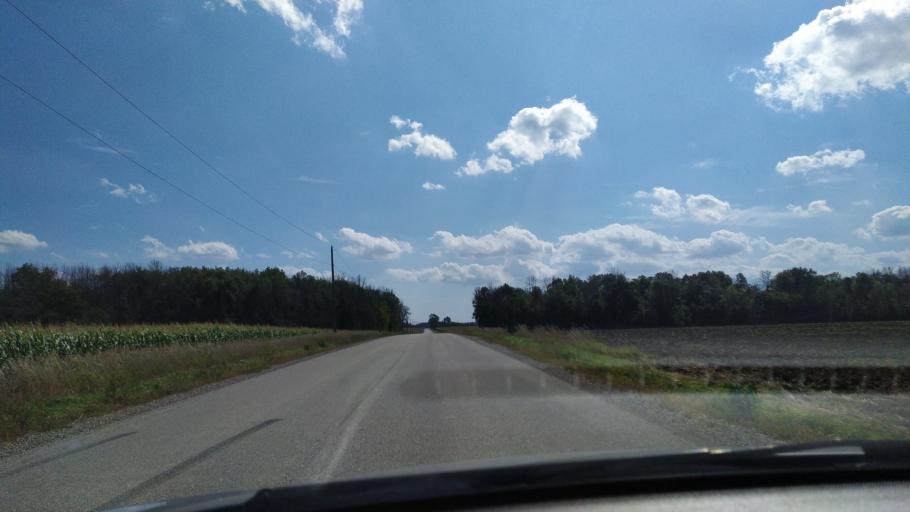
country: CA
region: Ontario
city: Stratford
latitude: 43.3096
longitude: -80.9479
